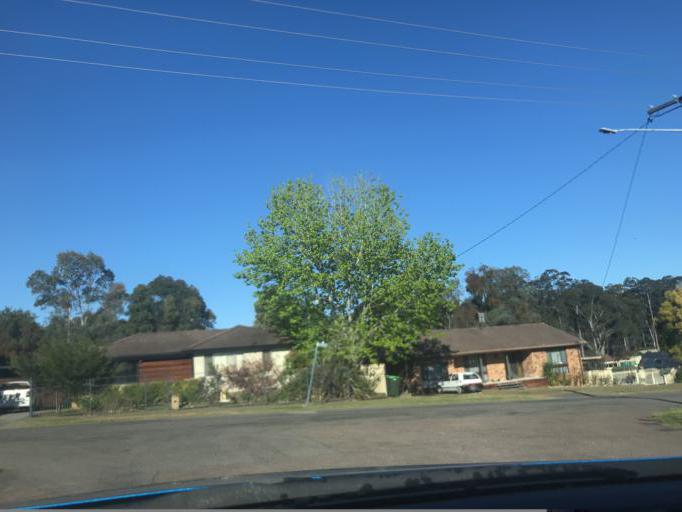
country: AU
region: New South Wales
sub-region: Cessnock
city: Cessnock
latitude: -32.9050
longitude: 151.2851
